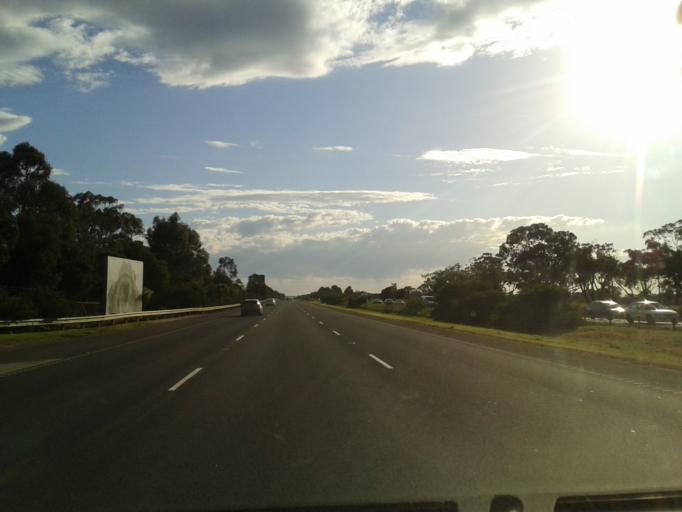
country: AU
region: Victoria
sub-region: Wyndham
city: Werribee
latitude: -37.9187
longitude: 144.6619
